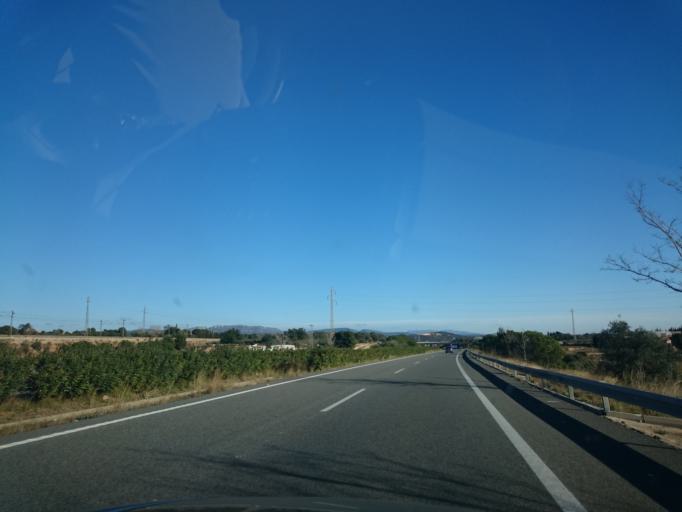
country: ES
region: Catalonia
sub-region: Provincia de Tarragona
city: Amposta
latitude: 40.7137
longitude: 0.5567
